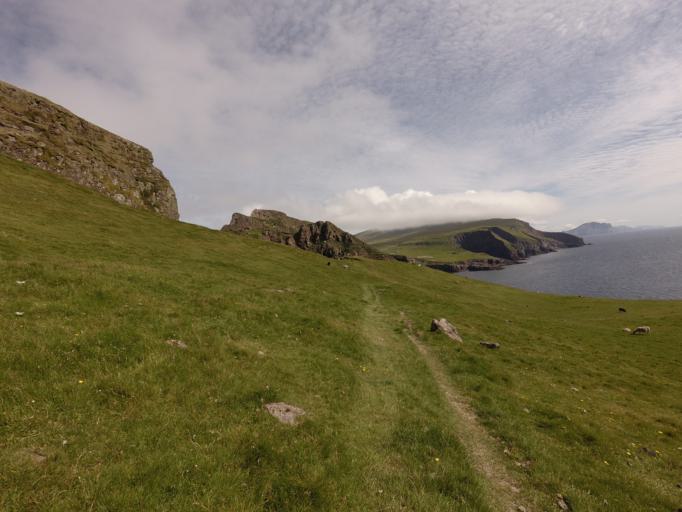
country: FO
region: Vagar
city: Sorvagur
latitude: 62.1008
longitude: -7.6655
